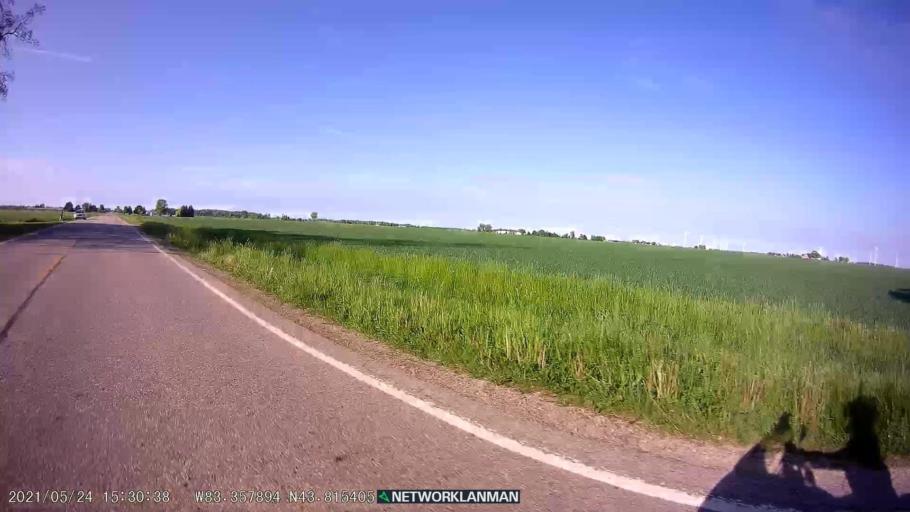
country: US
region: Michigan
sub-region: Huron County
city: Kilmanagh
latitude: 43.8154
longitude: -83.3581
